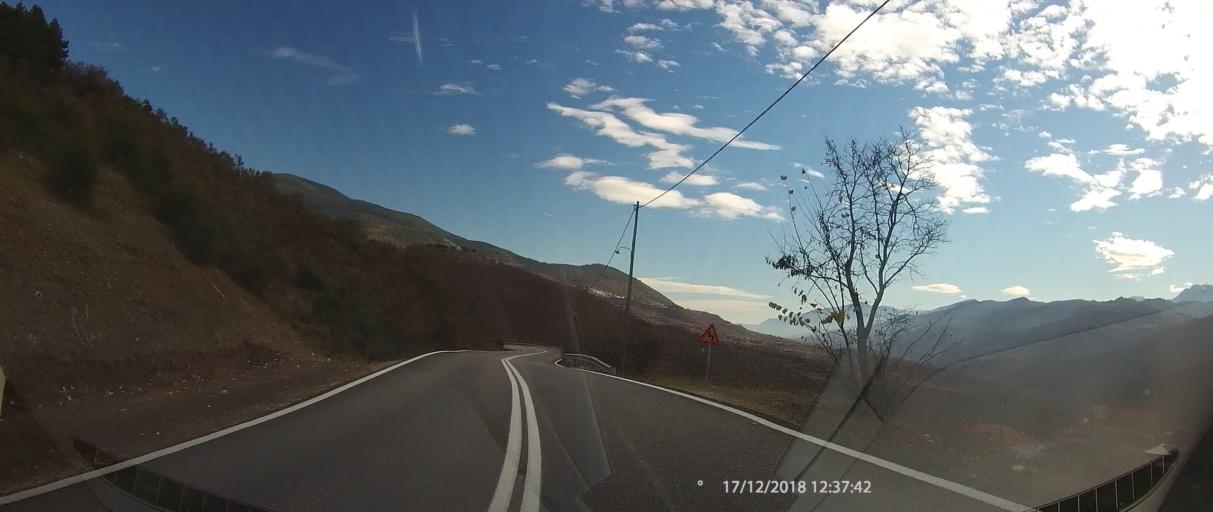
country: GR
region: Epirus
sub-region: Nomos Ioanninon
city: Metsovo
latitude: 39.8090
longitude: 21.3392
